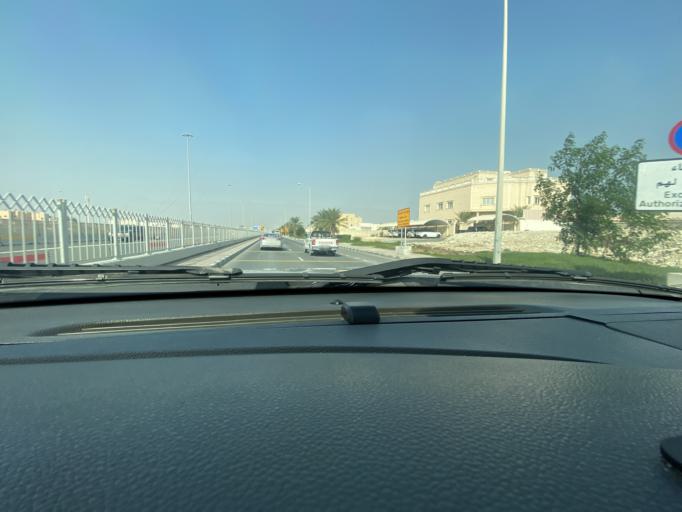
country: QA
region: Baladiyat ad Dawhah
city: Doha
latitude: 25.2453
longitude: 51.5147
